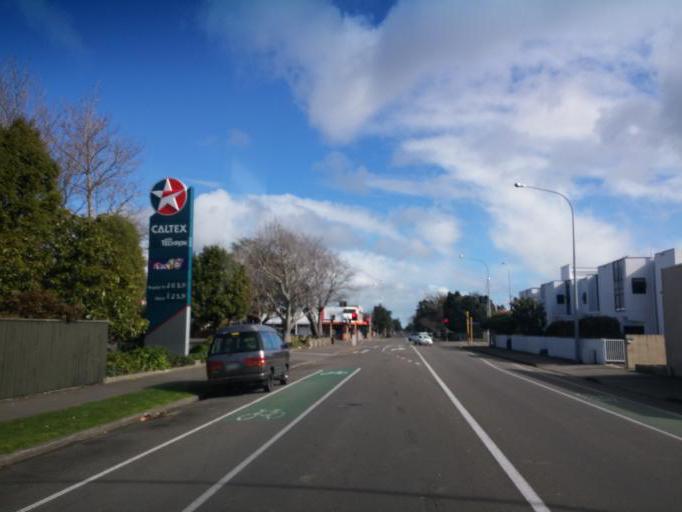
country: NZ
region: Manawatu-Wanganui
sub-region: Palmerston North City
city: Palmerston North
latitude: -40.3618
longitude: 175.6168
